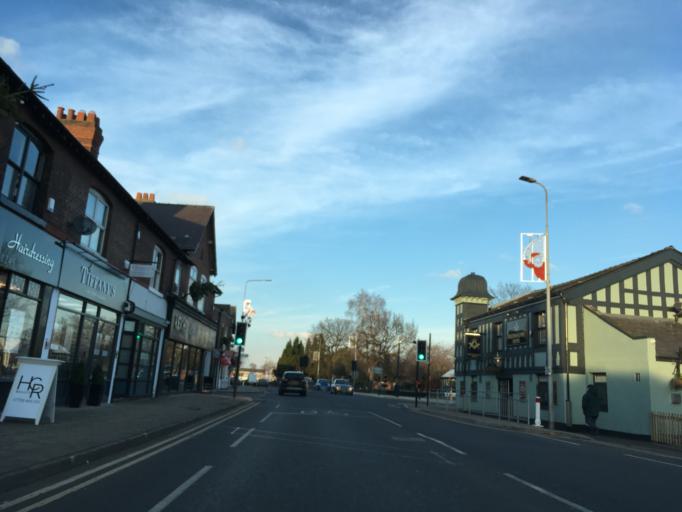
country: GB
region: England
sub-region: Cheshire East
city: Wilmslow
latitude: 53.3468
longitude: -2.2155
